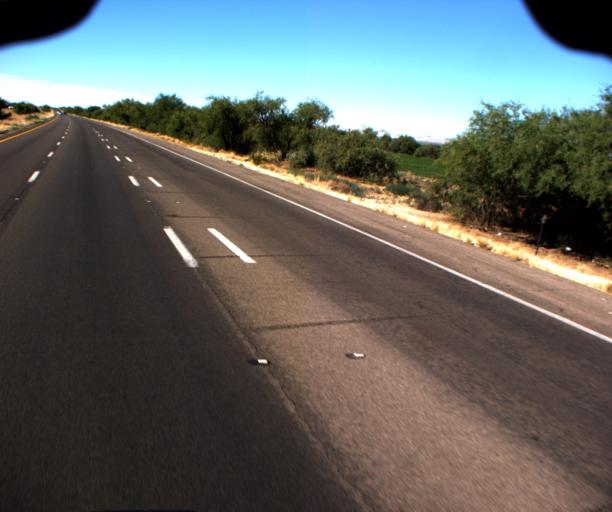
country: US
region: Arizona
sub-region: Pima County
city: Drexel Heights
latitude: 32.1015
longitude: -110.9935
